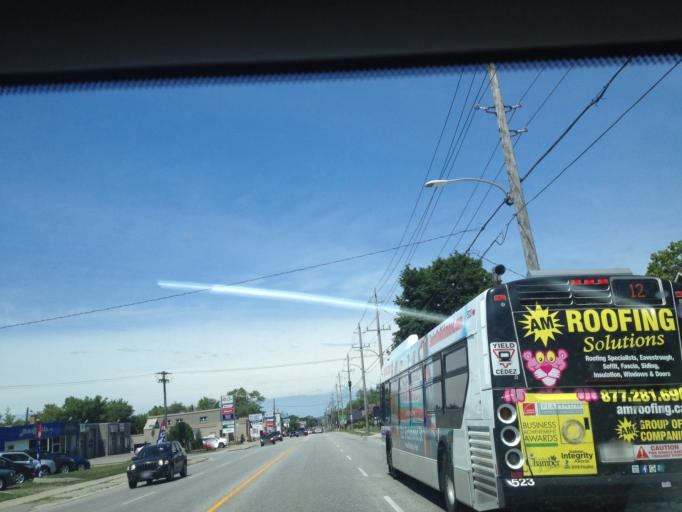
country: CA
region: Ontario
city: London
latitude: 42.9643
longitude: -81.2614
